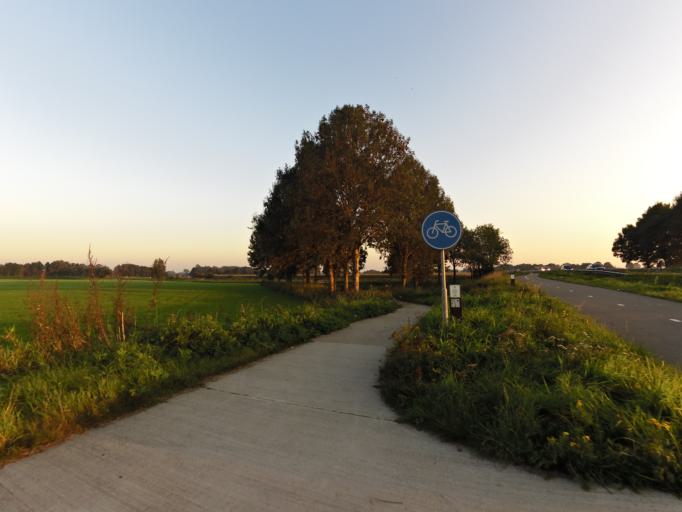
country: NL
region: Gelderland
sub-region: Gemeente Doetinchem
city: Doetinchem
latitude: 51.9371
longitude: 6.3142
